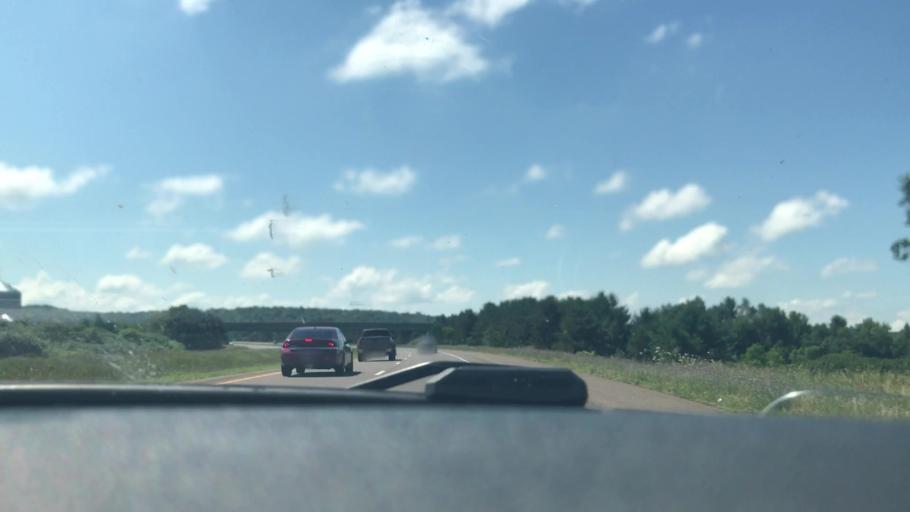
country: US
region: Wisconsin
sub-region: Chippewa County
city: Chippewa Falls
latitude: 44.9901
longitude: -91.4432
